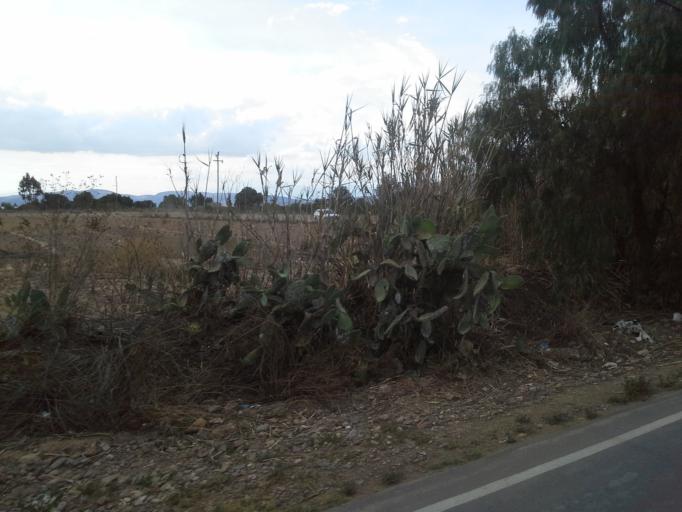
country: BO
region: Cochabamba
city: Tarata
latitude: -17.5788
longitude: -66.0152
